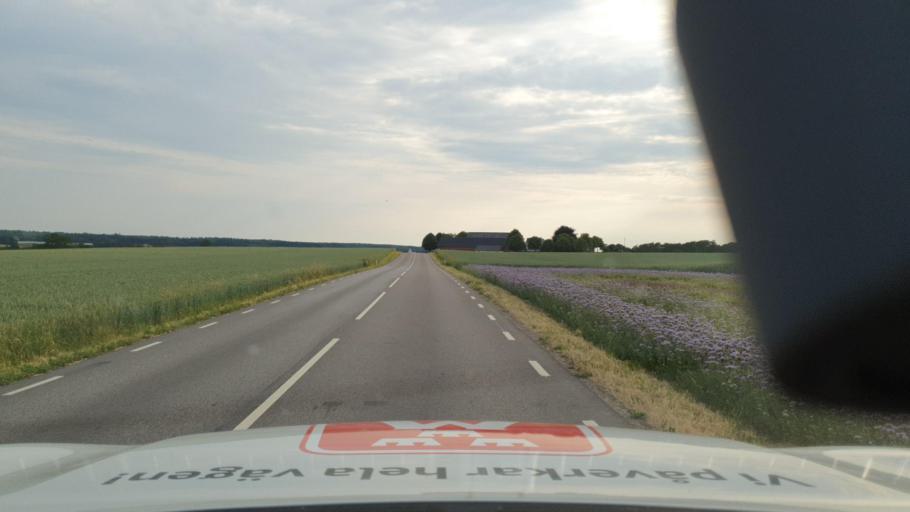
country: SE
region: Skane
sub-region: Sjobo Kommun
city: Sjoebo
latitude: 55.6441
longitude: 13.7928
